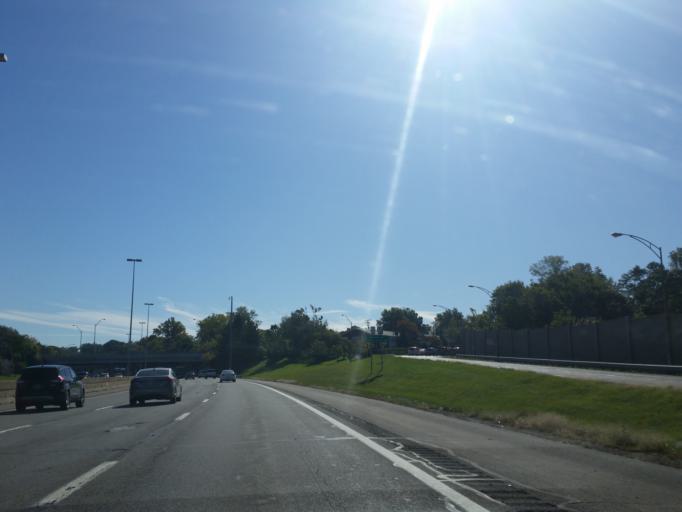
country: US
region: Ohio
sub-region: Cuyahoga County
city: Rocky River
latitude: 41.4734
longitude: -81.8604
